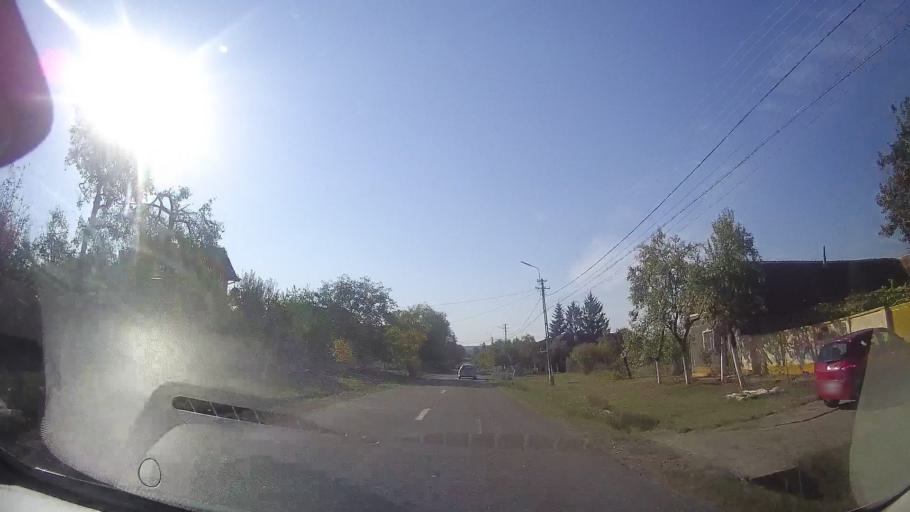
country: RO
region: Timis
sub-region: Oras Recas
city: Recas
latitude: 45.8630
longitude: 21.5149
